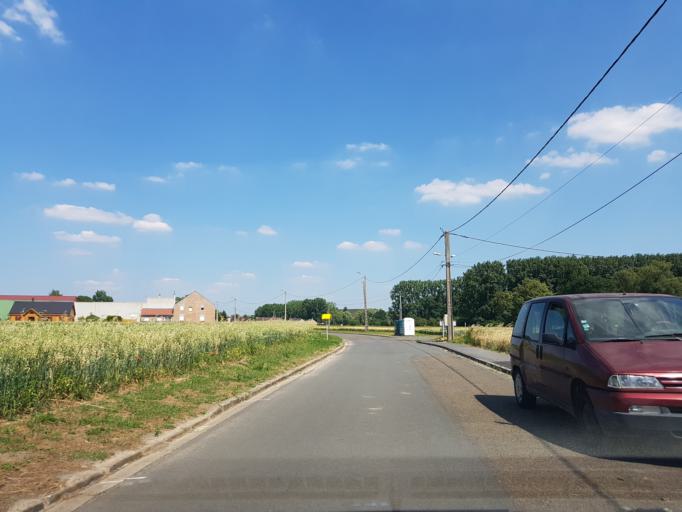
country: FR
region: Nord-Pas-de-Calais
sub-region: Departement du Nord
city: Roeulx
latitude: 50.3026
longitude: 3.3291
